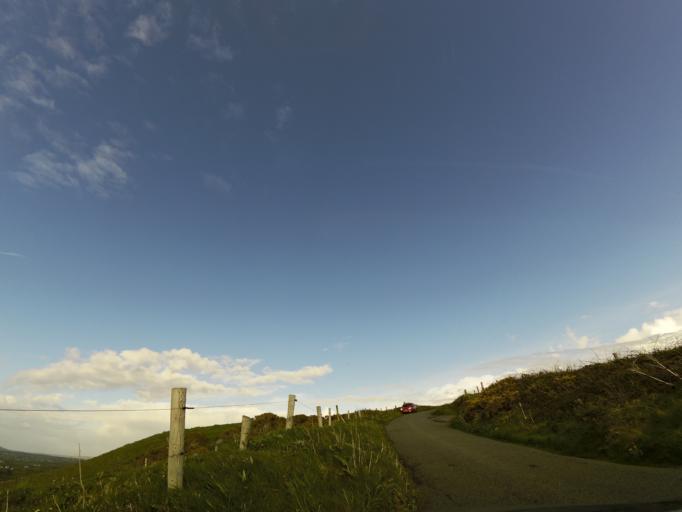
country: IE
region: Connaught
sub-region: County Galway
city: Bearna
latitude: 53.0031
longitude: -9.3860
